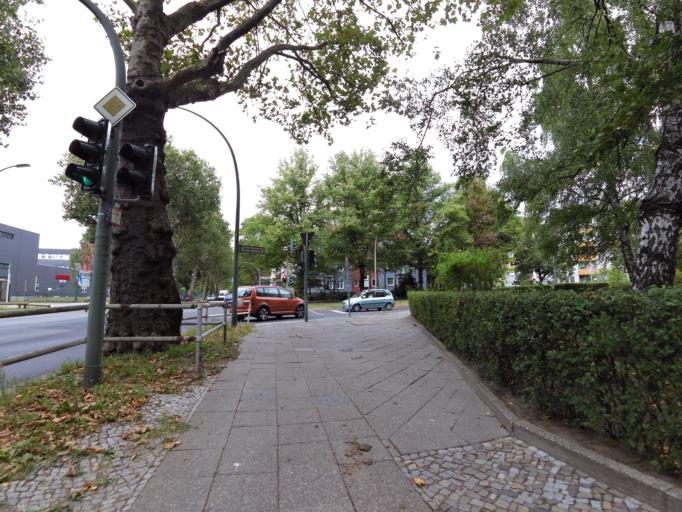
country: DE
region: Berlin
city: Mariendorf
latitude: 52.4433
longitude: 13.3759
